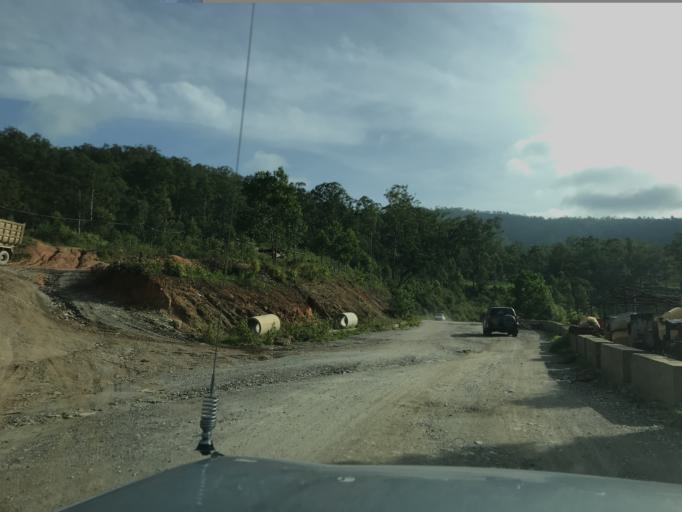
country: TL
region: Aileu
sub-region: Aileu Villa
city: Aileu
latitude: -8.6638
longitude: 125.5428
